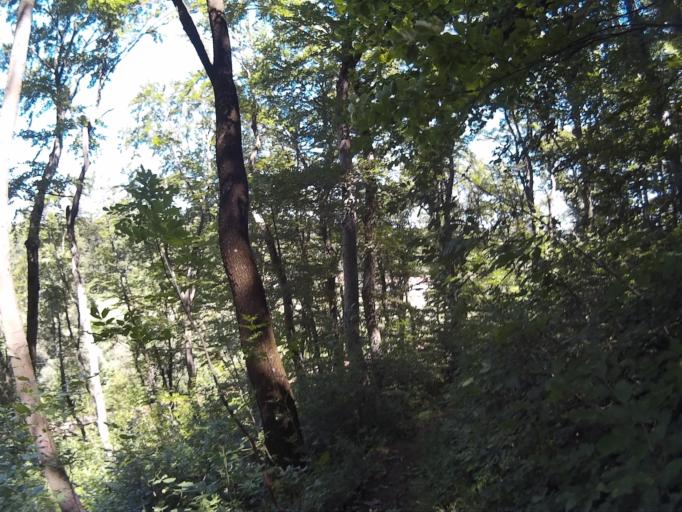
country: HU
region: Veszprem
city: Urkut
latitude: 47.1365
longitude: 17.6378
